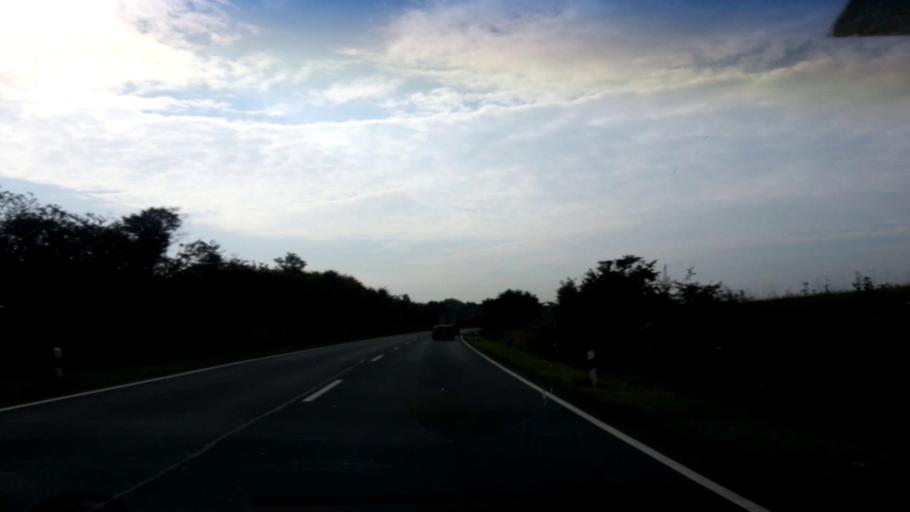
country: DE
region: Bavaria
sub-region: Regierungsbezirk Unterfranken
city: Prichsenstadt
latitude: 49.8393
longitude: 10.3530
